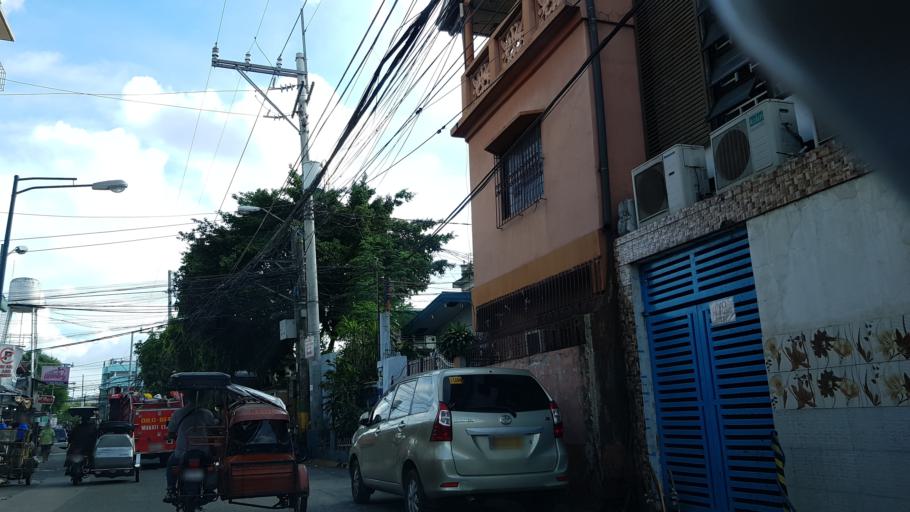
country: PH
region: Calabarzon
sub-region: Province of Rizal
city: Pateros
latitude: 14.5484
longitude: 121.0596
